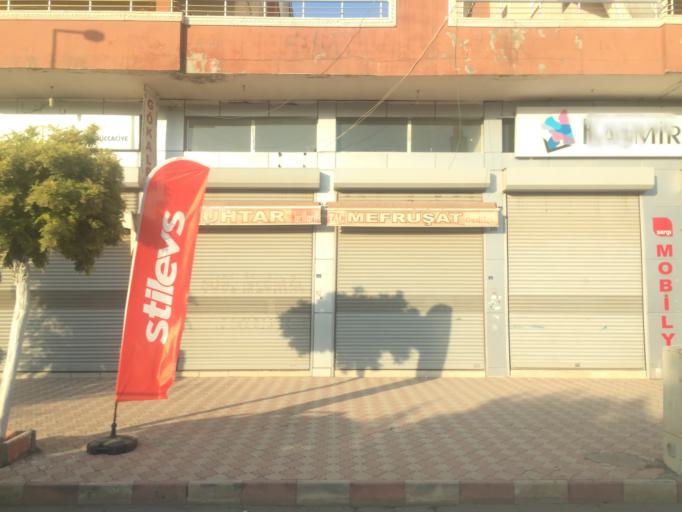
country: TR
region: Mardin
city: Midyat
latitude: 37.4284
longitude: 41.3391
